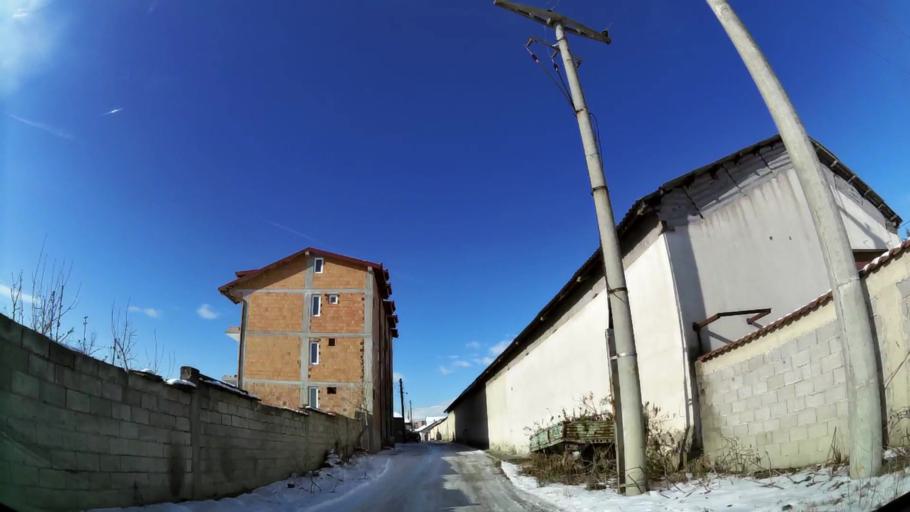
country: MK
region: Saraj
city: Saraj
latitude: 42.0011
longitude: 21.3346
